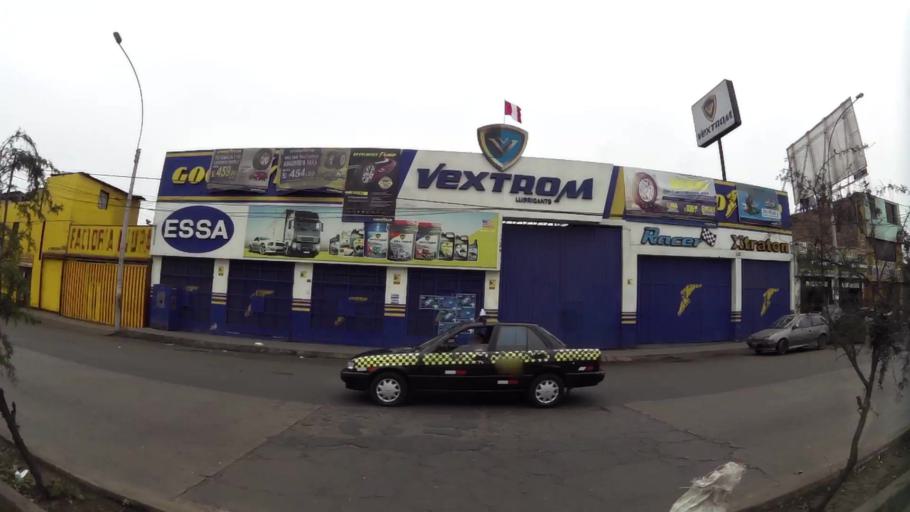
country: PE
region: Lima
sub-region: Lima
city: San Luis
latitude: -12.0764
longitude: -77.0170
